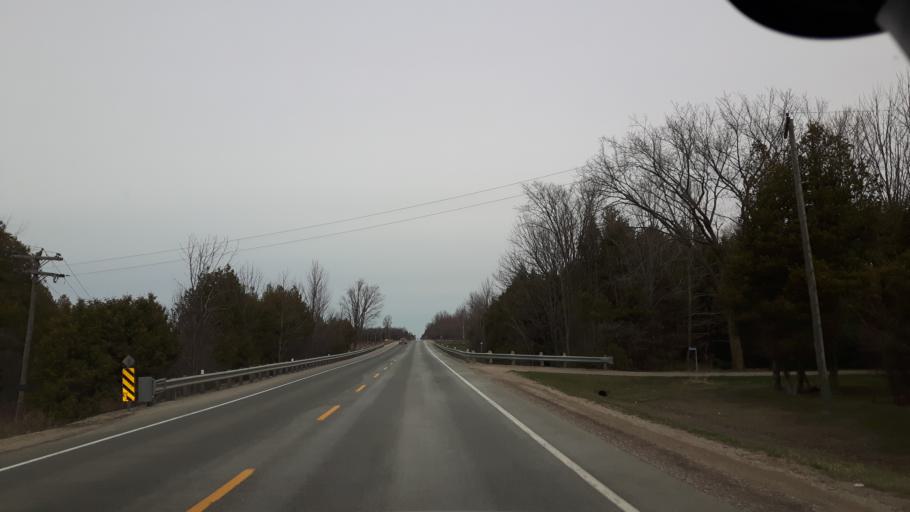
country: CA
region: Ontario
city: Goderich
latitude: 43.6534
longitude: -81.7057
